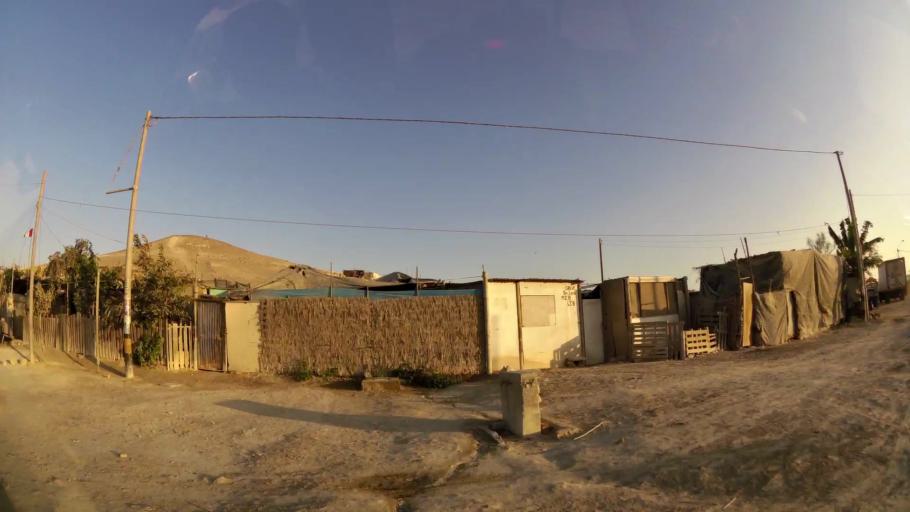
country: PE
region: Ica
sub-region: Provincia de Pisco
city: Villa Tupac Amaru
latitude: -13.6982
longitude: -76.1566
